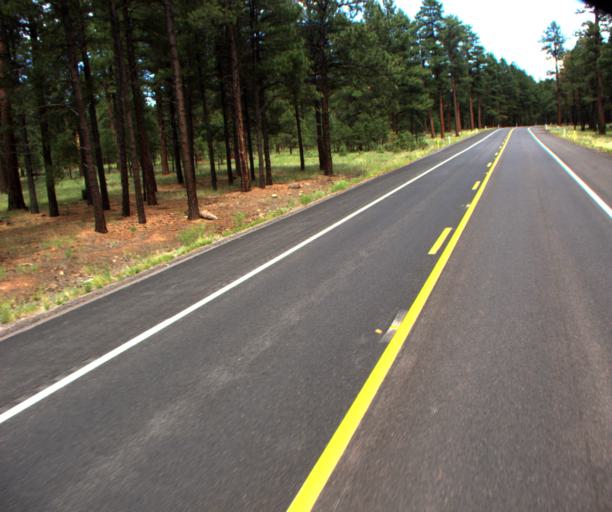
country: US
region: Arizona
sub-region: Coconino County
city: Flagstaff
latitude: 35.2683
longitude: -111.7107
